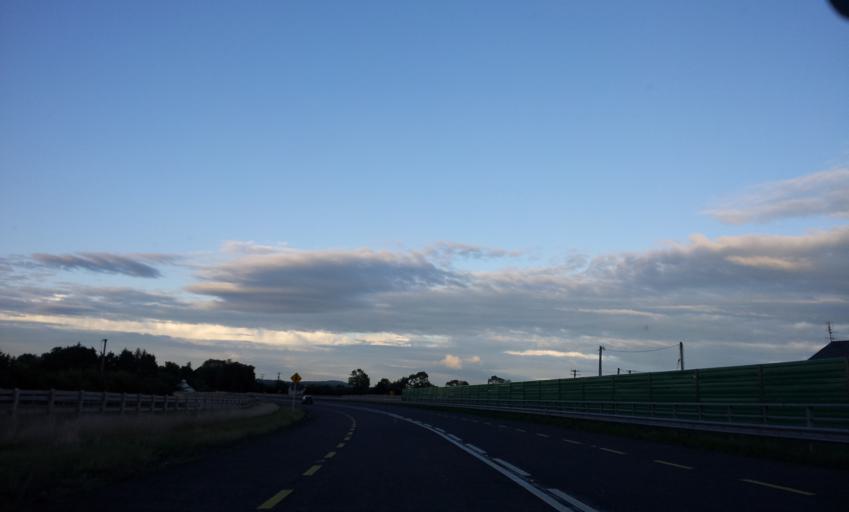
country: IE
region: Munster
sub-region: County Limerick
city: Newcastle West
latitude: 52.4363
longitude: -9.0953
